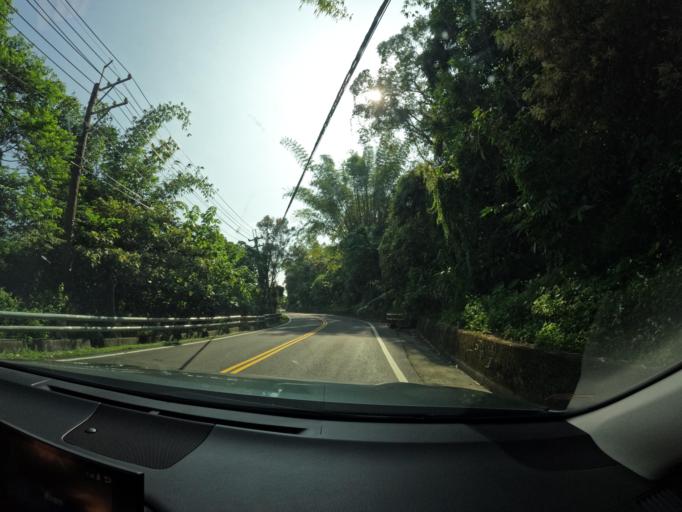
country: TW
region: Taiwan
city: Yujing
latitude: 23.0780
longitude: 120.6200
